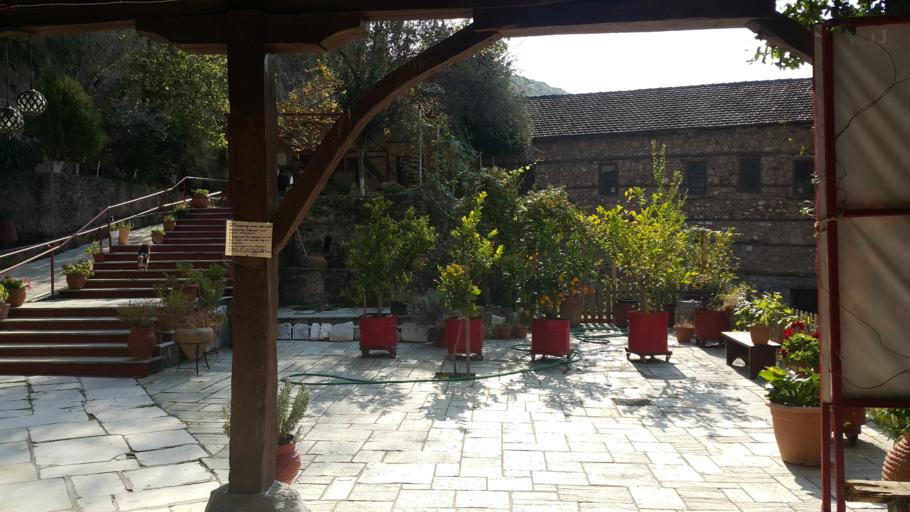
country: GR
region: Central Macedonia
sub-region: Nomos Imathias
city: Veroia
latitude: 40.4586
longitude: 22.2393
